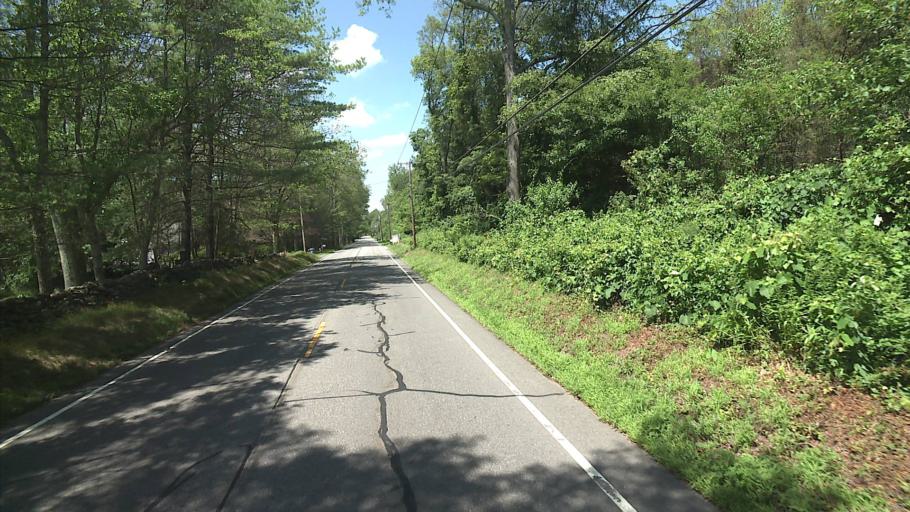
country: US
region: Connecticut
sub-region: Windham County
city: Plainfield Village
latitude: 41.7096
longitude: -72.0261
